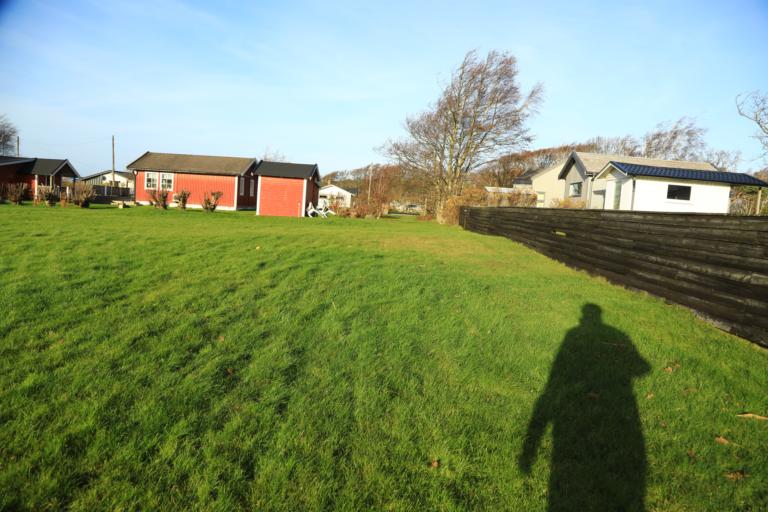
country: SE
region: Halland
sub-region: Varbergs Kommun
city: Varberg
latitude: 57.1816
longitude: 12.2164
